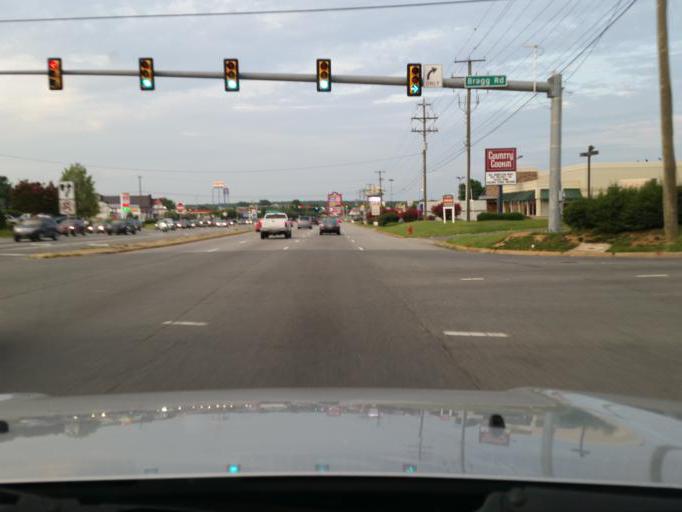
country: US
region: Virginia
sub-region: Stafford County
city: Falmouth
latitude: 38.2940
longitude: -77.5187
